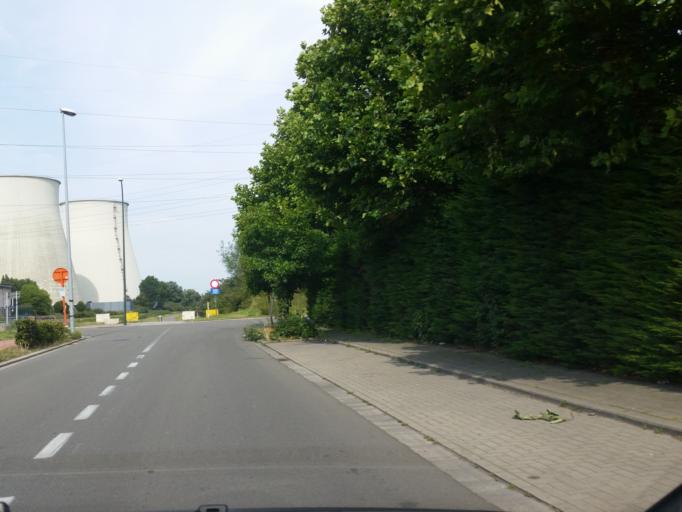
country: BE
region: Flanders
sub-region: Provincie Vlaams-Brabant
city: Vilvoorde
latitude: 50.9383
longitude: 4.4227
